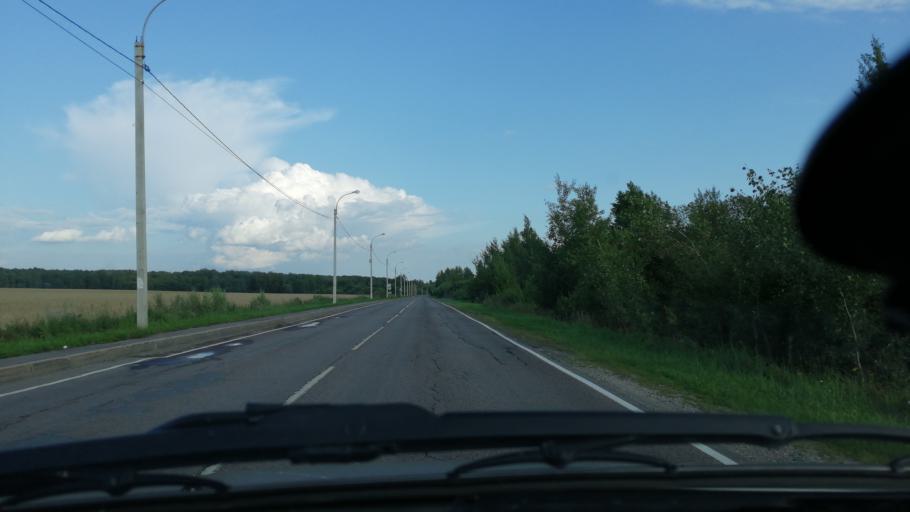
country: RU
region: Moskovskaya
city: Troitskoye
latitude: 55.2884
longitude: 38.5347
